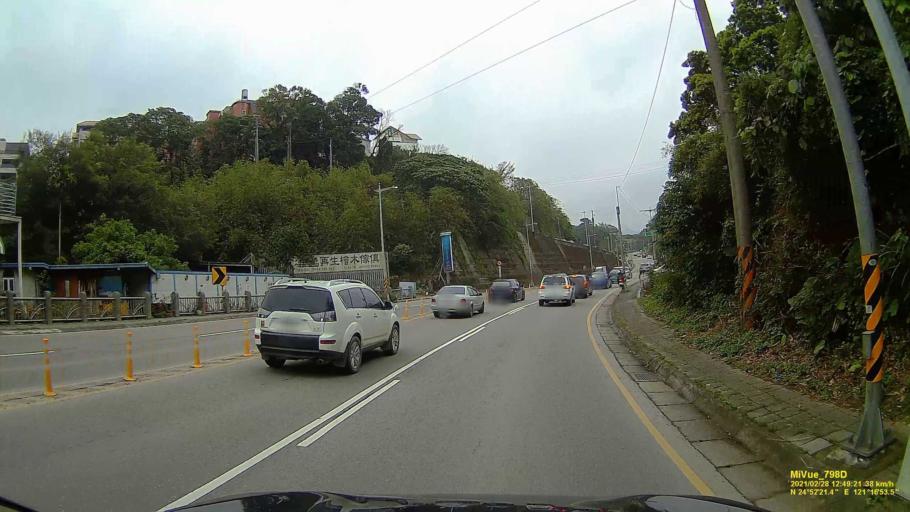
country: TW
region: Taiwan
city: Daxi
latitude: 24.8724
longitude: 121.2816
